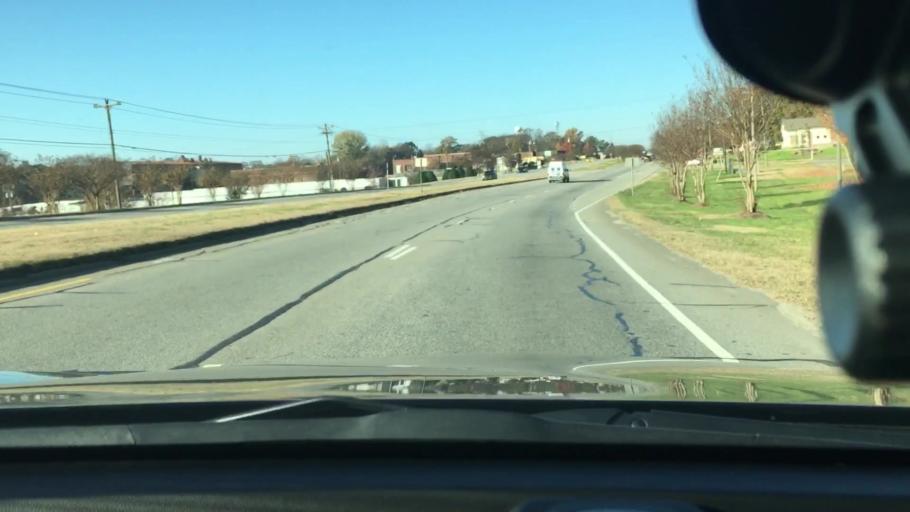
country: US
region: North Carolina
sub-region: Cabarrus County
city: Harrisburg
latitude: 35.3161
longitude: -80.6780
